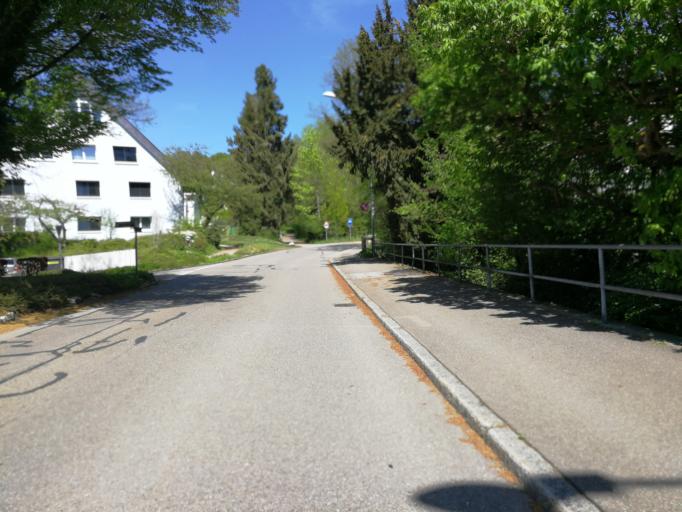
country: CH
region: Zurich
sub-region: Bezirk Meilen
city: Uetikon
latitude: 47.2665
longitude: 8.6850
